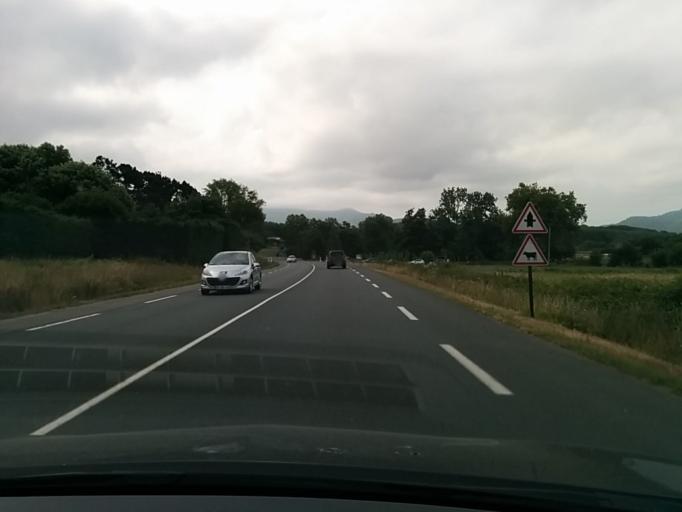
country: FR
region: Aquitaine
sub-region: Departement des Pyrenees-Atlantiques
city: Ciboure
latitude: 43.3761
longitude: -1.6864
